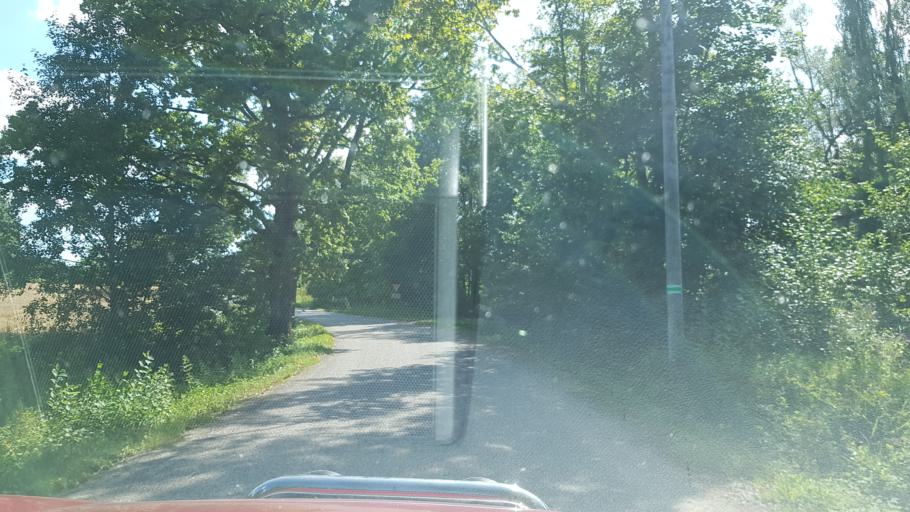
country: EE
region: Vorumaa
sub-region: Voru linn
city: Voru
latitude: 57.7455
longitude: 27.1082
